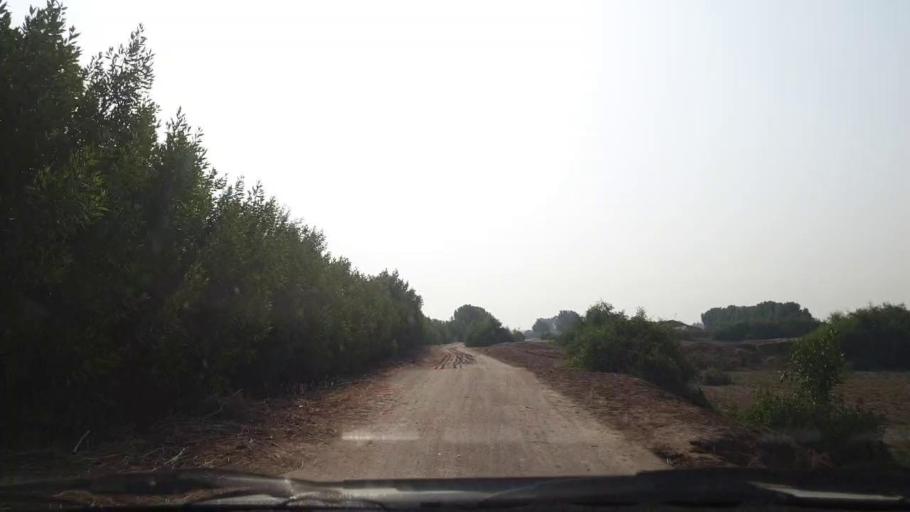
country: PK
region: Sindh
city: Tando Muhammad Khan
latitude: 25.0040
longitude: 68.4525
